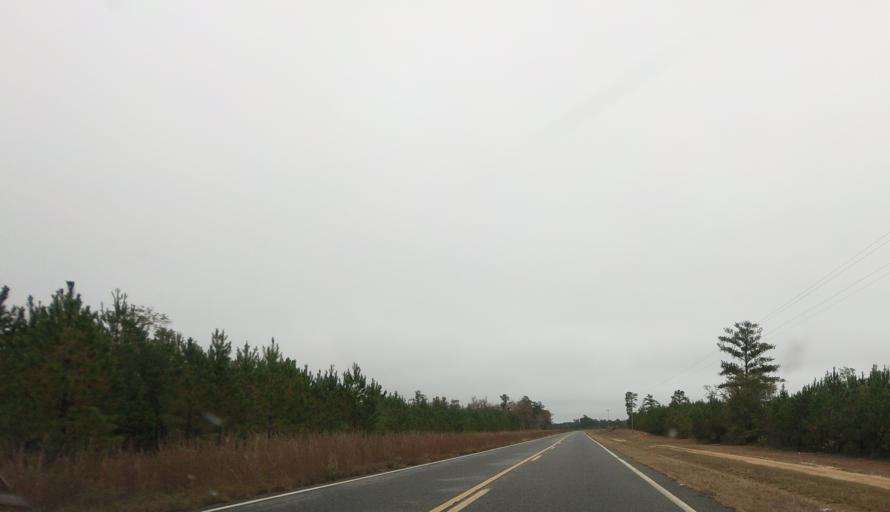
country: US
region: Georgia
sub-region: Taylor County
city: Butler
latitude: 32.4325
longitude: -84.3122
